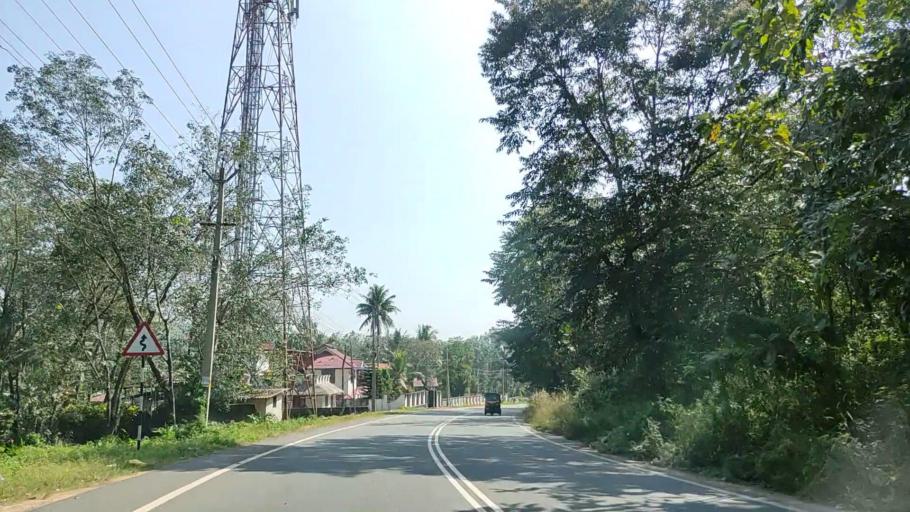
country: IN
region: Kerala
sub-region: Kollam
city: Punalur
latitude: 8.9205
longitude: 77.0360
